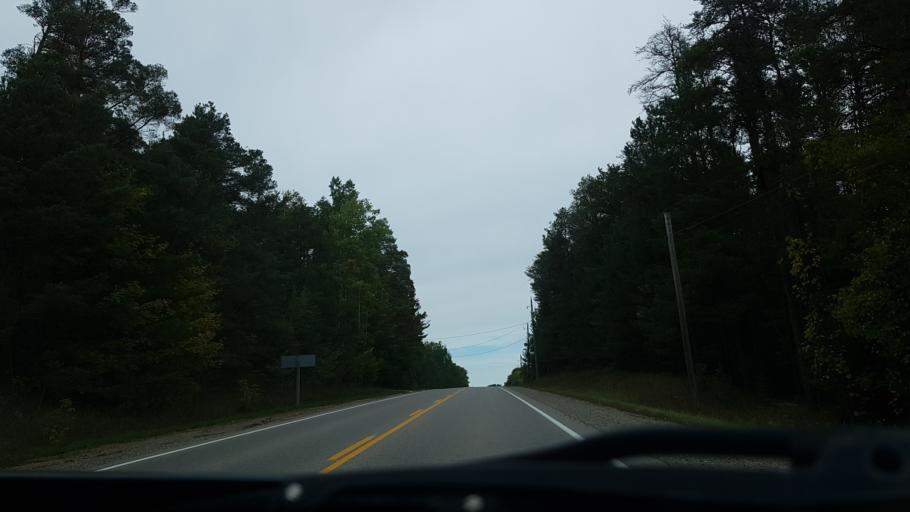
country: CA
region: Ontario
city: Orangeville
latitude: 44.0087
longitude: -80.0008
